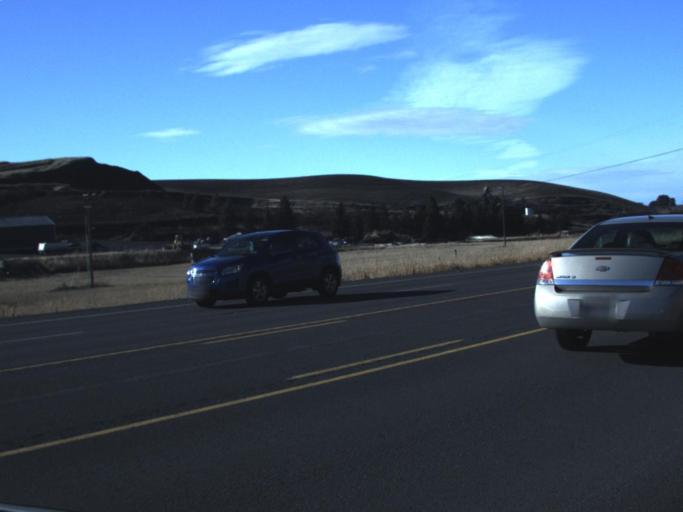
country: US
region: Washington
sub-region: Whitman County
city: Pullman
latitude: 46.7280
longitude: -117.1087
